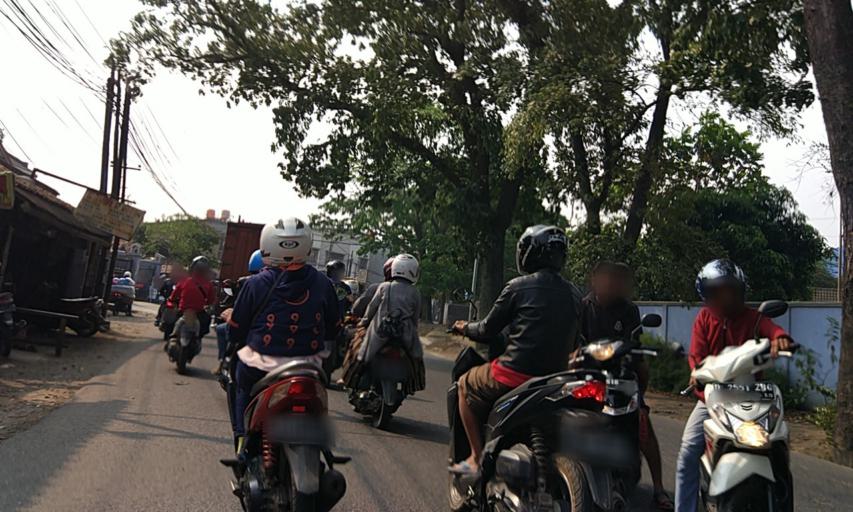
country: ID
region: West Java
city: Margahayukencana
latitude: -6.9783
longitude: 107.5611
